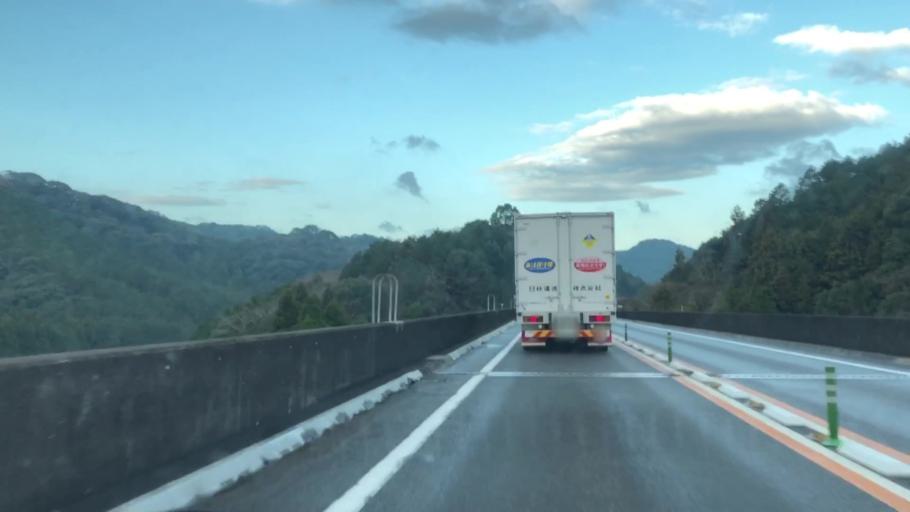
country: JP
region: Saga Prefecture
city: Ureshinomachi-shimojuku
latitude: 33.1567
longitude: 129.9194
